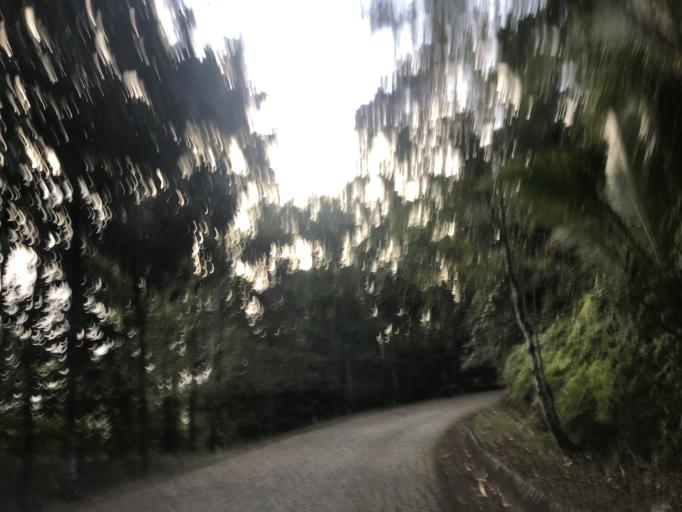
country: BR
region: Bahia
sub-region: Gandu
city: Gandu
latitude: -13.9123
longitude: -39.4636
